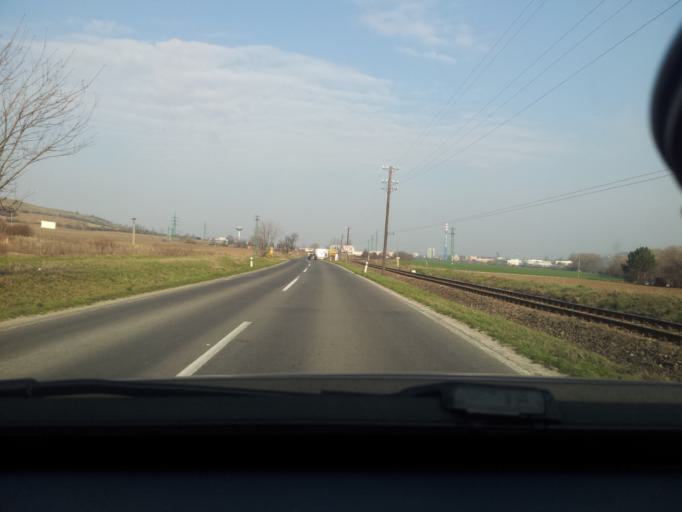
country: SK
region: Trnavsky
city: Hlohovec
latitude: 48.4133
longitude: 17.8337
